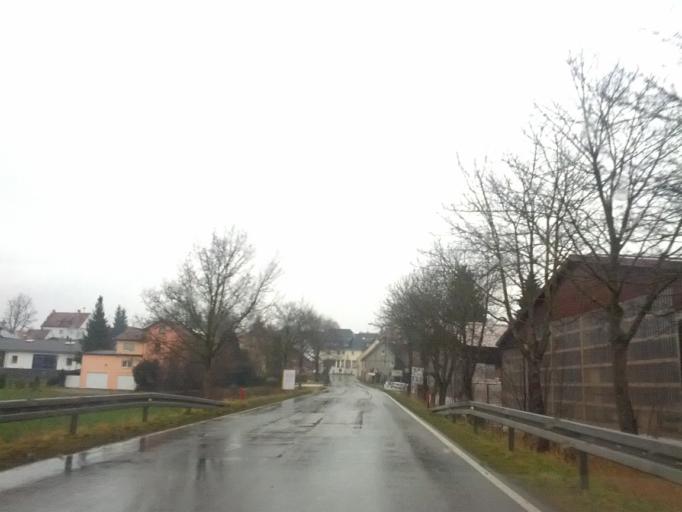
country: DE
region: Baden-Wuerttemberg
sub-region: Tuebingen Region
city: Rot an der Rot
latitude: 48.0146
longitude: 10.0252
